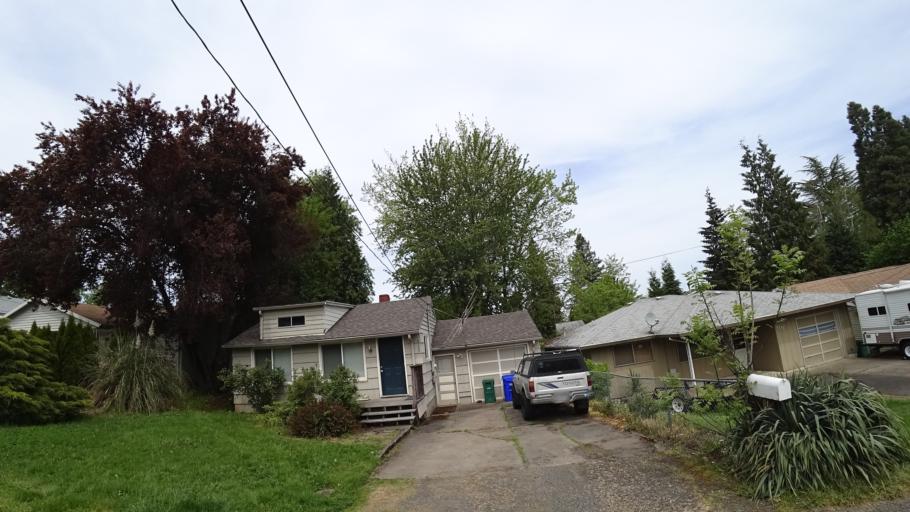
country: US
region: Oregon
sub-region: Clackamas County
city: Milwaukie
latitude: 45.4501
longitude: -122.6195
